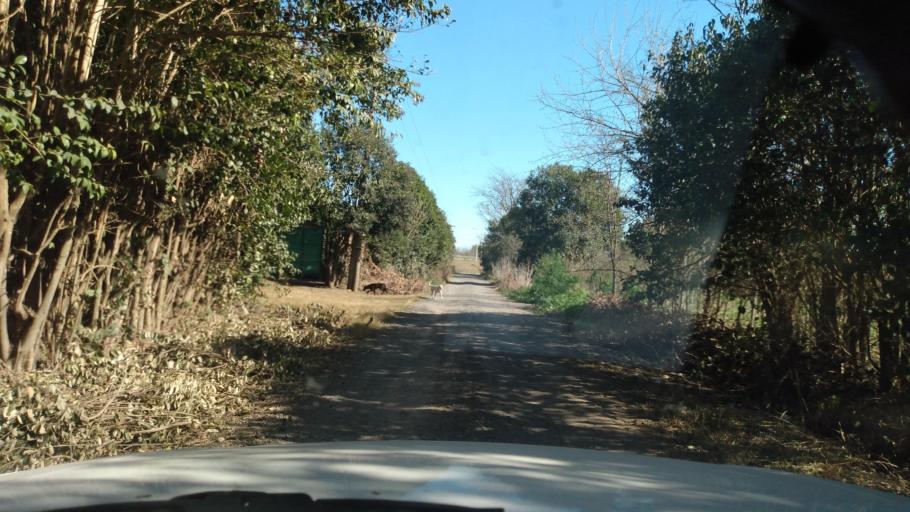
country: AR
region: Buenos Aires
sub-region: Partido de Mercedes
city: Mercedes
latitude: -34.6624
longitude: -59.3988
